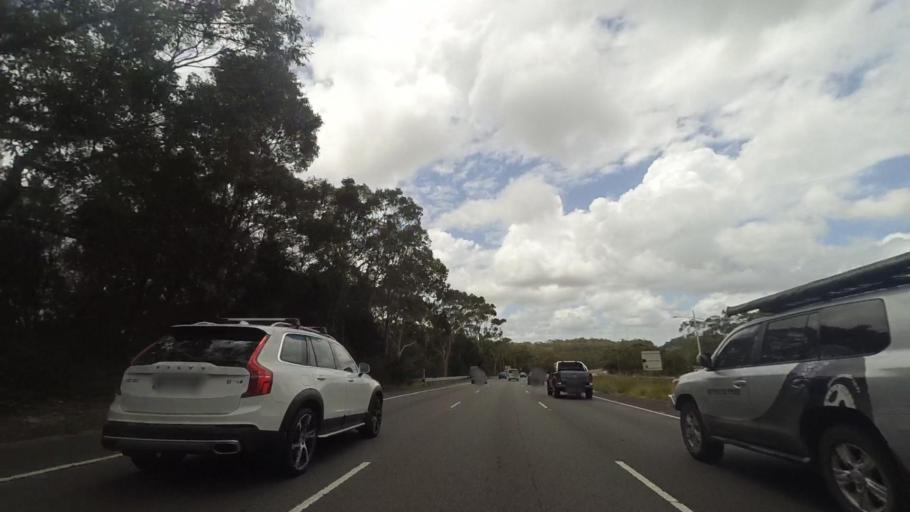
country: AU
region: New South Wales
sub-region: Gosford Shire
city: Umina
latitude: -33.4637
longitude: 151.1952
